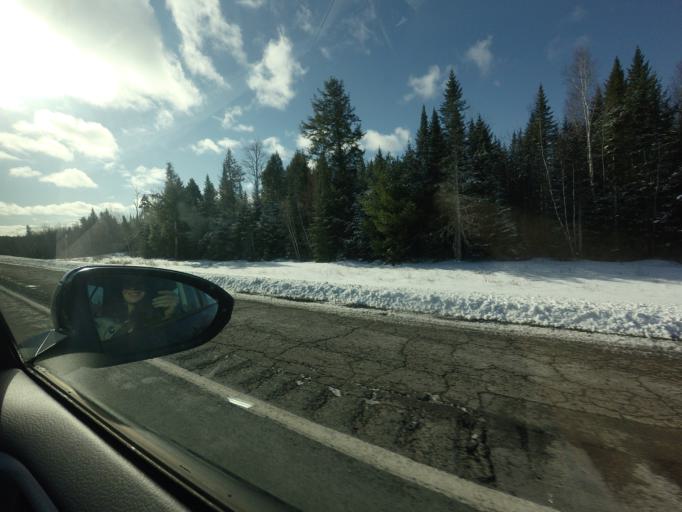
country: CA
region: New Brunswick
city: Fredericton
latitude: 45.8844
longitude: -66.6398
